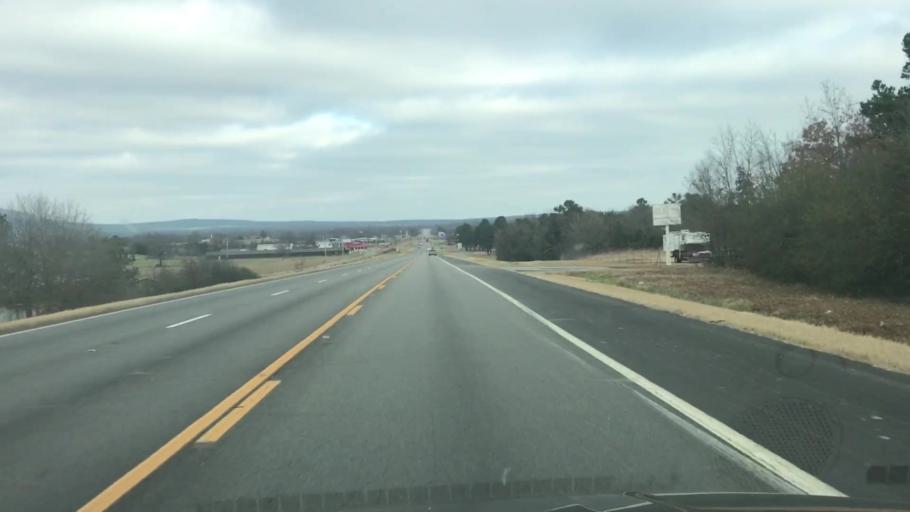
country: US
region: Arkansas
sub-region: Scott County
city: Waldron
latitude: 34.8905
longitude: -94.1077
